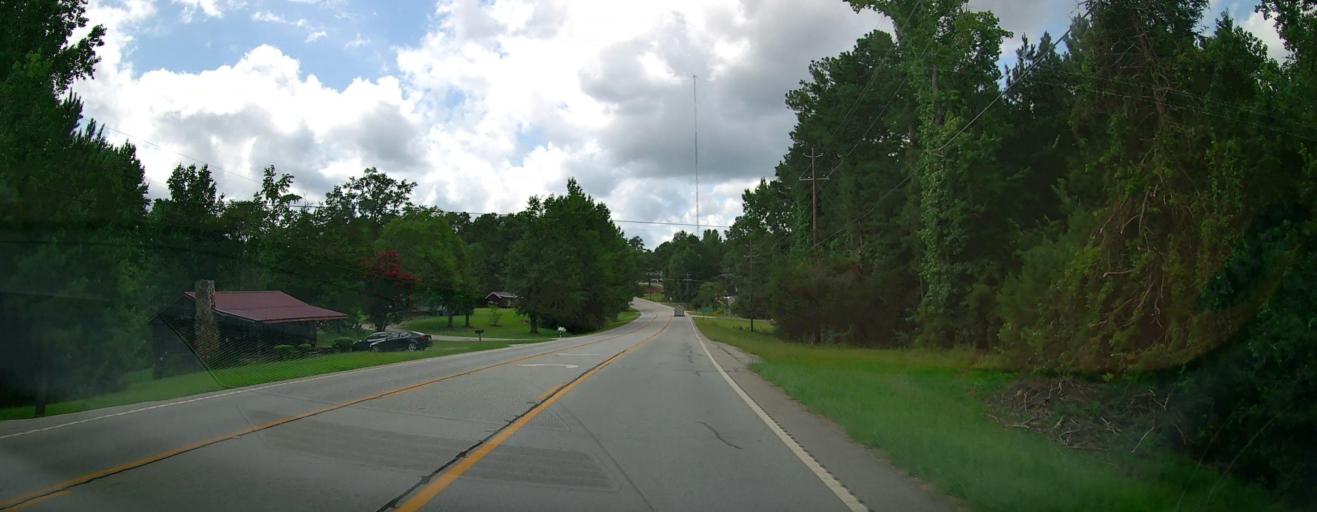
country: US
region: Georgia
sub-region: Heard County
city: Franklin
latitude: 33.2668
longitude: -85.0823
